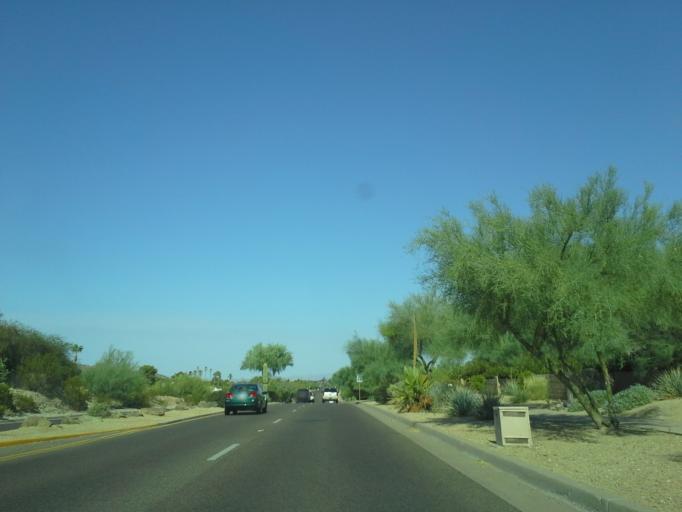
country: US
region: Arizona
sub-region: Maricopa County
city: Paradise Valley
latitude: 33.5315
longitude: -111.9892
